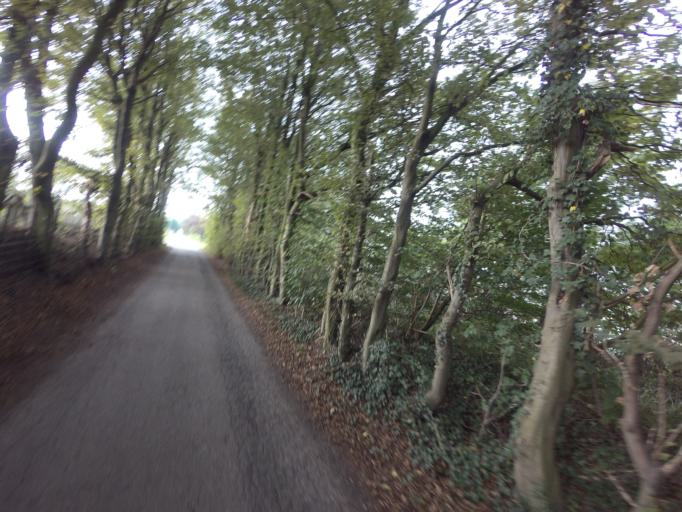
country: NL
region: Limburg
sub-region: Eijsden-Margraten
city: Margraten
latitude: 50.8212
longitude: 5.8364
